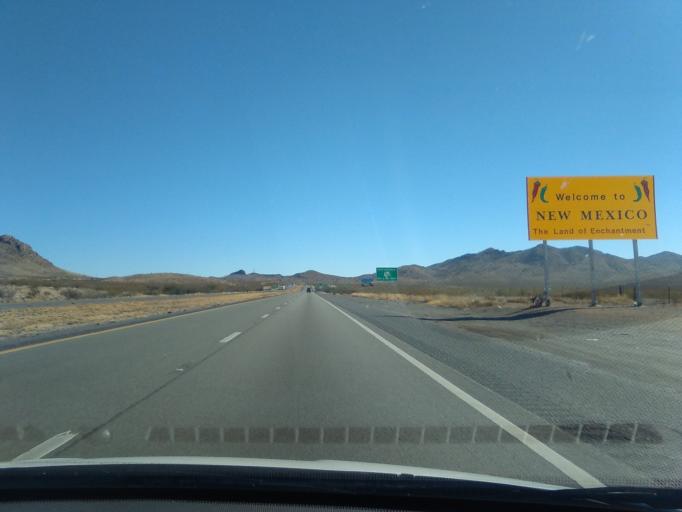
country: US
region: New Mexico
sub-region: Hidalgo County
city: Lordsburg
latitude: 32.2271
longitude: -109.0480
